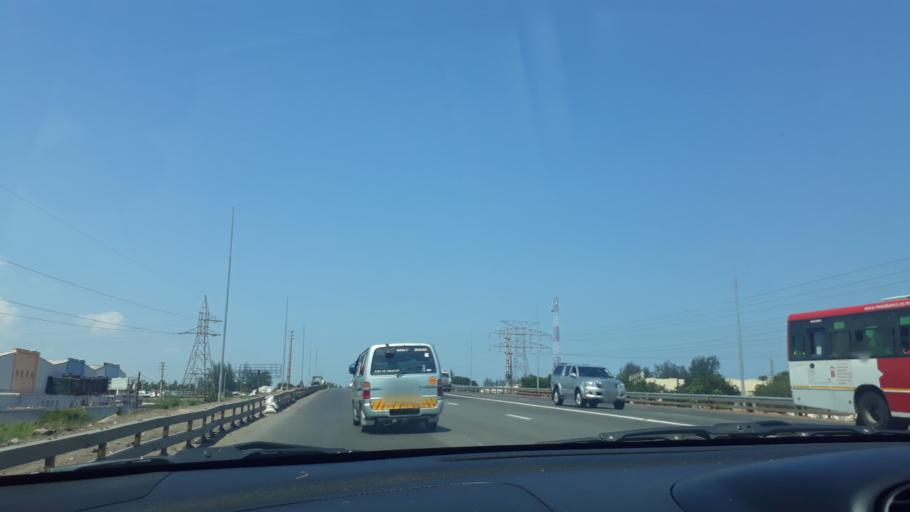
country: MZ
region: Maputo
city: Matola
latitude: -25.9389
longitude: 32.4900
